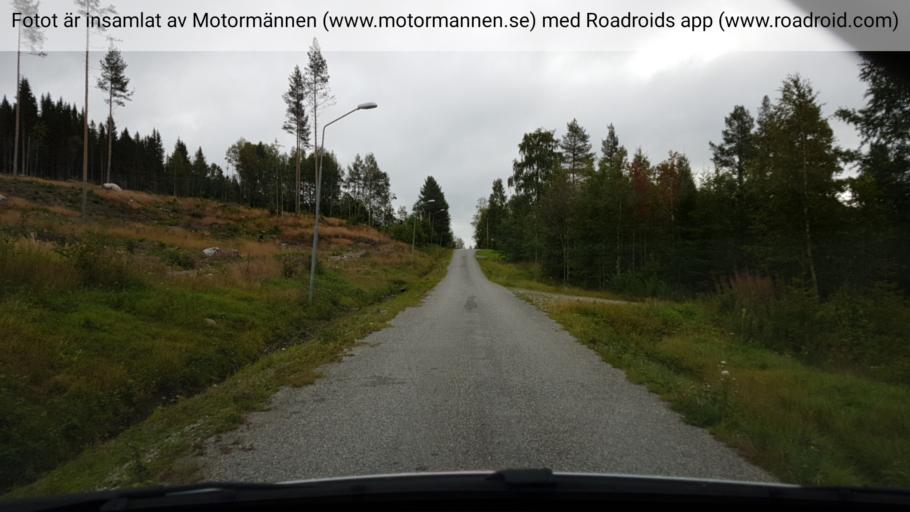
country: SE
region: Vaesterbotten
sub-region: Dorotea Kommun
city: Dorotea
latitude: 63.8589
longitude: 16.3646
